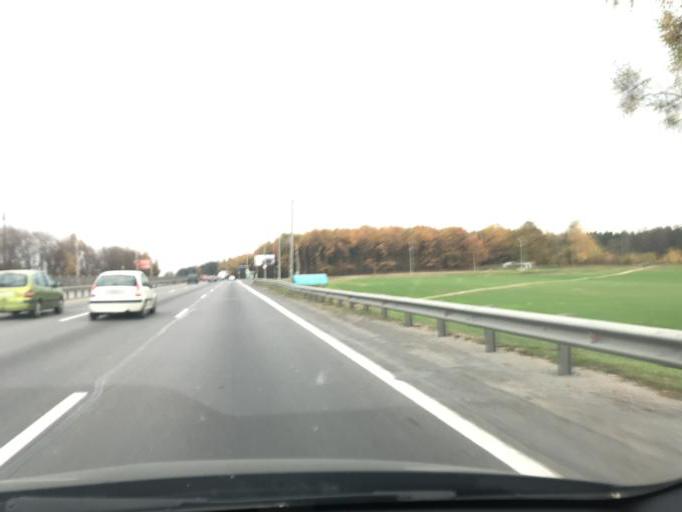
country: BY
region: Minsk
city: Hatava
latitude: 53.8335
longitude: 27.6351
